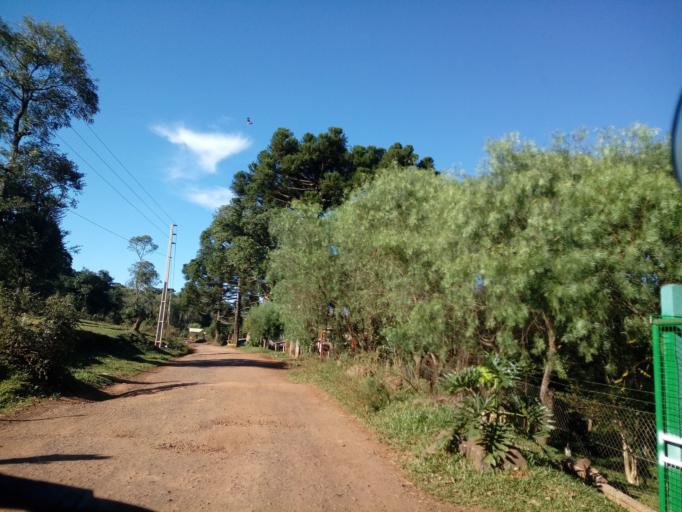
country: BR
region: Santa Catarina
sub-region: Chapeco
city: Chapeco
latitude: -27.2006
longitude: -52.6765
